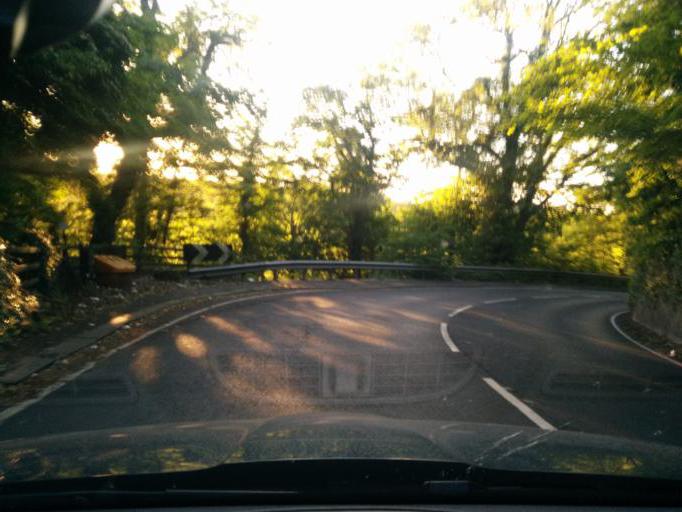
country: GB
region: England
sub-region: Northumberland
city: Bedlington
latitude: 55.1243
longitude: -1.5818
